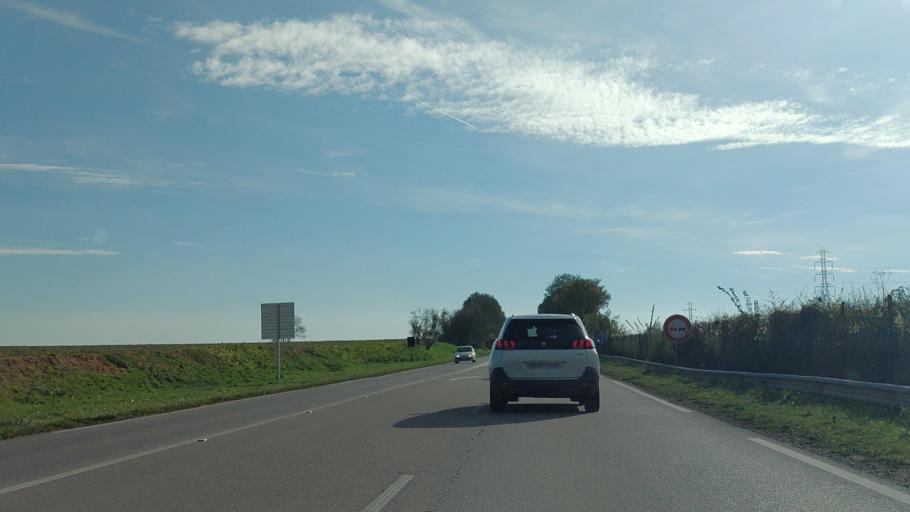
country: FR
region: Ile-de-France
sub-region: Departement du Val-d'Oise
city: Survilliers
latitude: 49.0827
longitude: 2.5297
